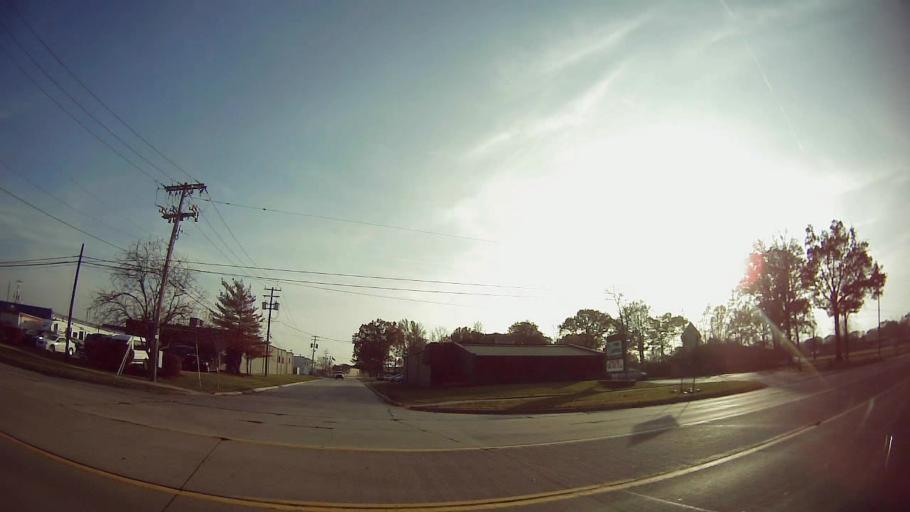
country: US
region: Michigan
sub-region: Macomb County
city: Fraser
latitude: 42.5241
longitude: -82.9532
